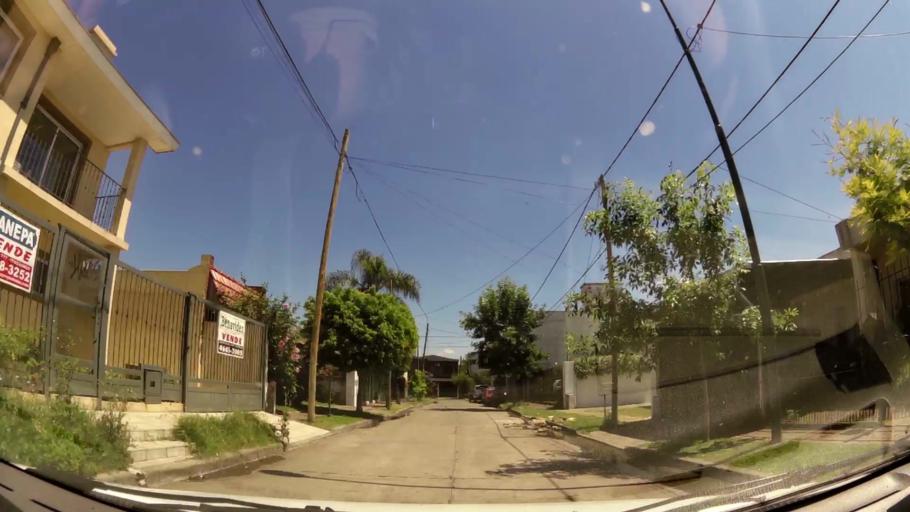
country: AR
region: Buenos Aires
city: Ituzaingo
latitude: -34.6596
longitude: -58.6771
